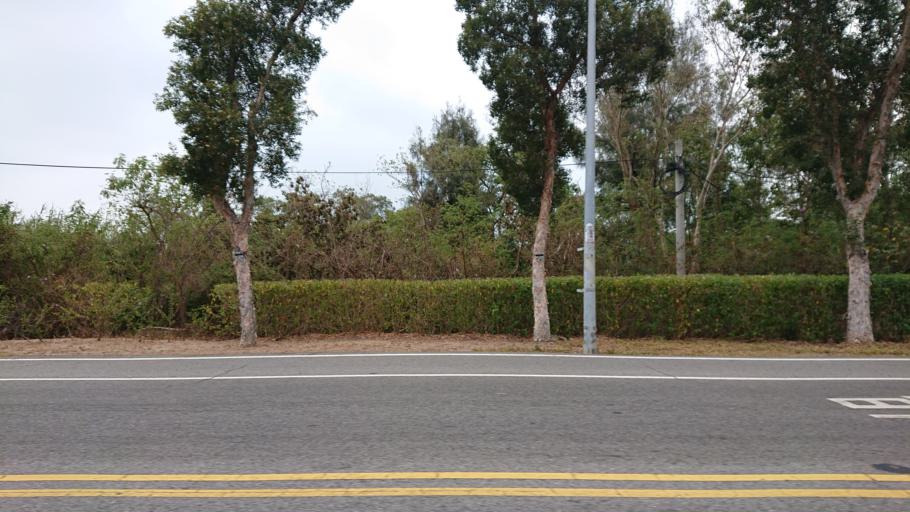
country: TW
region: Fukien
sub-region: Kinmen
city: Jincheng
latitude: 24.4382
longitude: 118.4007
